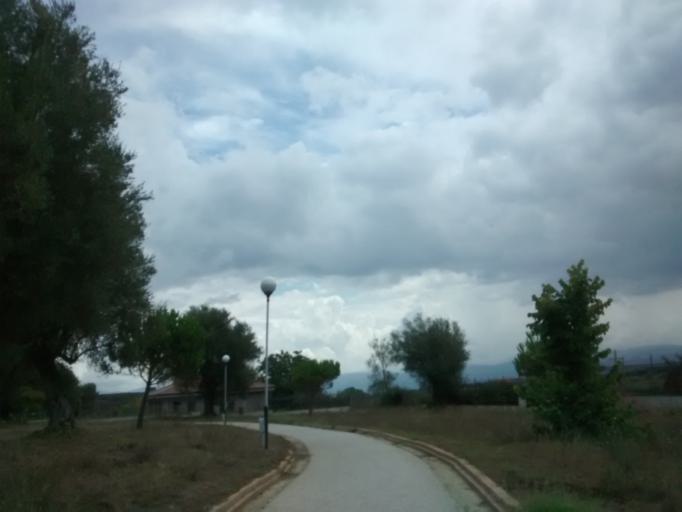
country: IT
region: Calabria
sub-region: Provincia di Vibo-Valentia
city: Vibo Valentia
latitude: 38.6630
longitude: 16.0804
